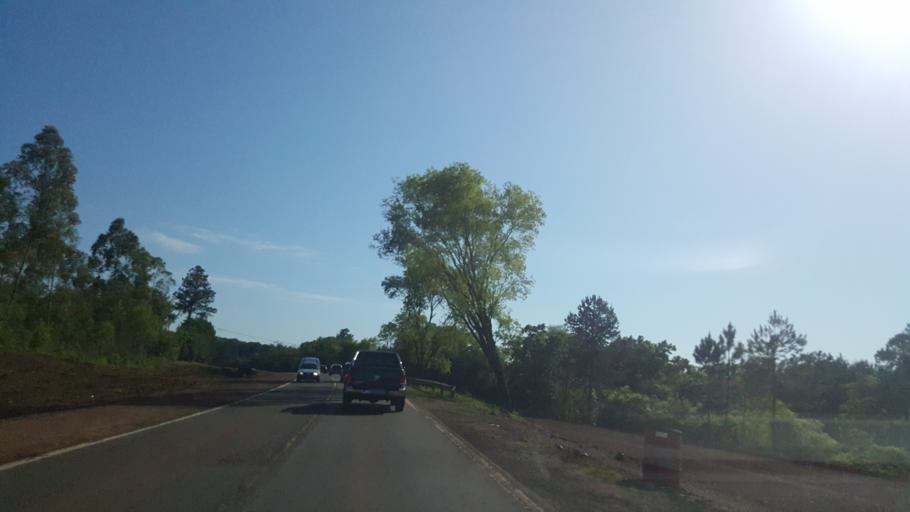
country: AR
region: Misiones
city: Santa Ana
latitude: -27.3671
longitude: -55.5600
